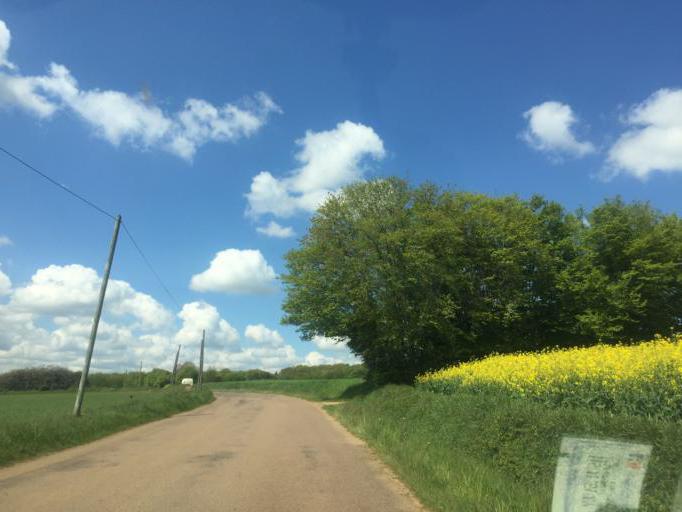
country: FR
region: Bourgogne
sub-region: Departement de l'Yonne
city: Fontenailles
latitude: 47.4832
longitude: 3.3935
